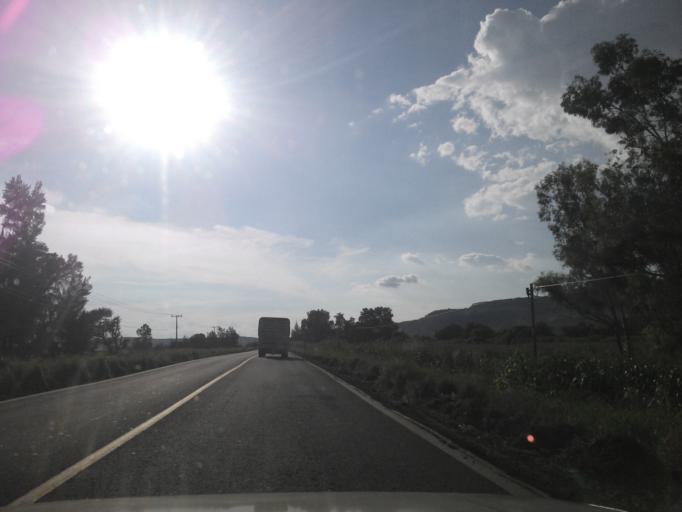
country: MX
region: Jalisco
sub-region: Atotonilco el Alto
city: San Francisco de Asis
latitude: 20.5436
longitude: -102.6088
